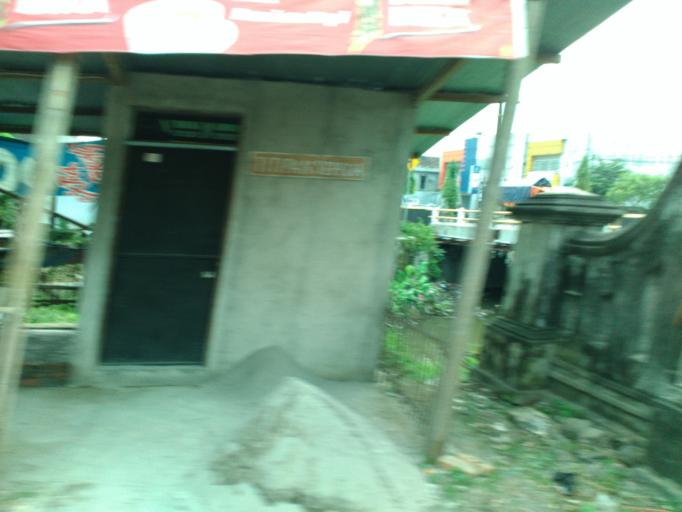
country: ID
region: Central Java
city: Gatak
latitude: -7.5969
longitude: 110.7031
